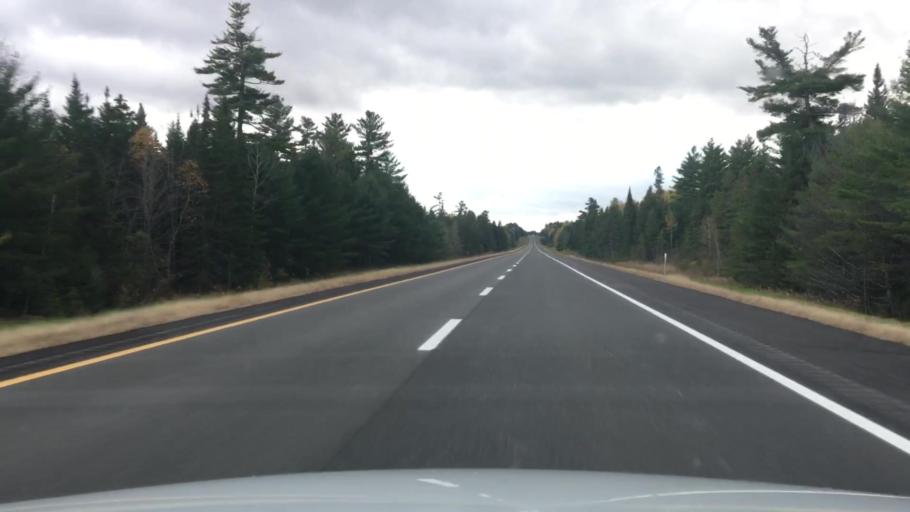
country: US
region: Maine
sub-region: Penobscot County
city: Patten
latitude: 46.0725
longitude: -68.2222
